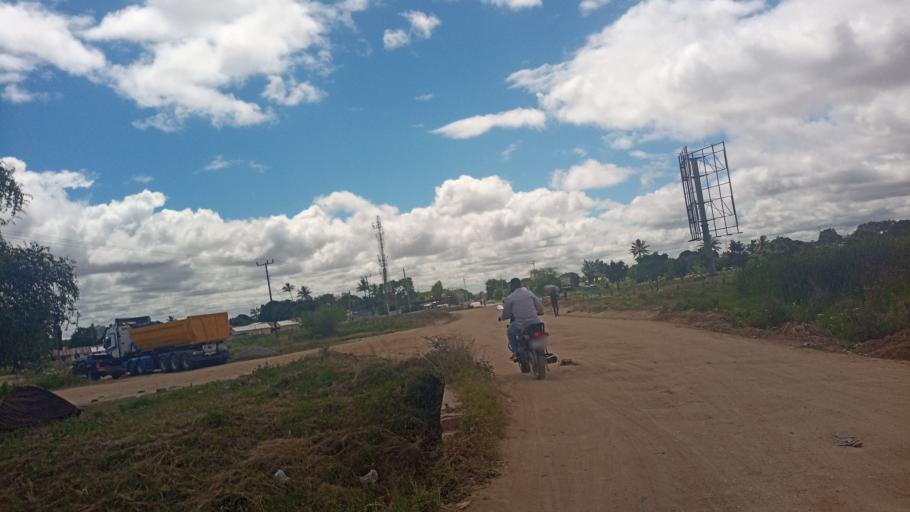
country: TZ
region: Dodoma
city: Dodoma
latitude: -6.1880
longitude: 35.7324
